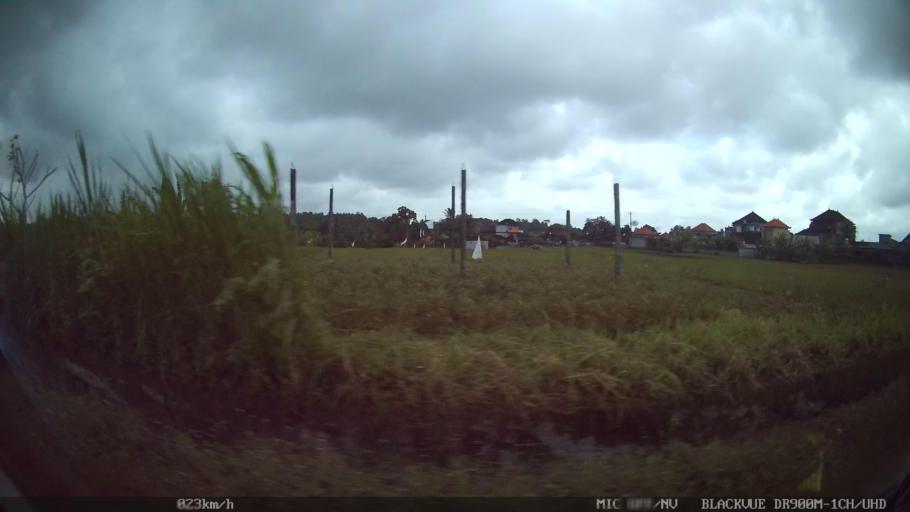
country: ID
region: Bali
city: Banjar Sempidi
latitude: -8.5220
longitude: 115.1948
